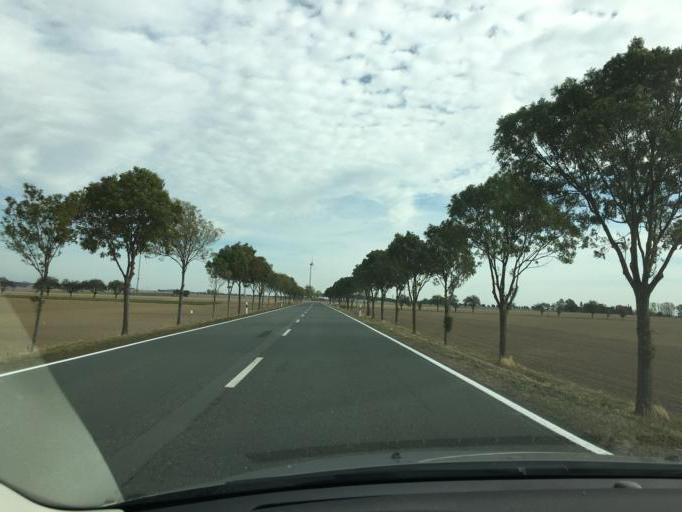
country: DE
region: Saxony
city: Stauchitz
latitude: 51.2792
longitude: 13.1818
